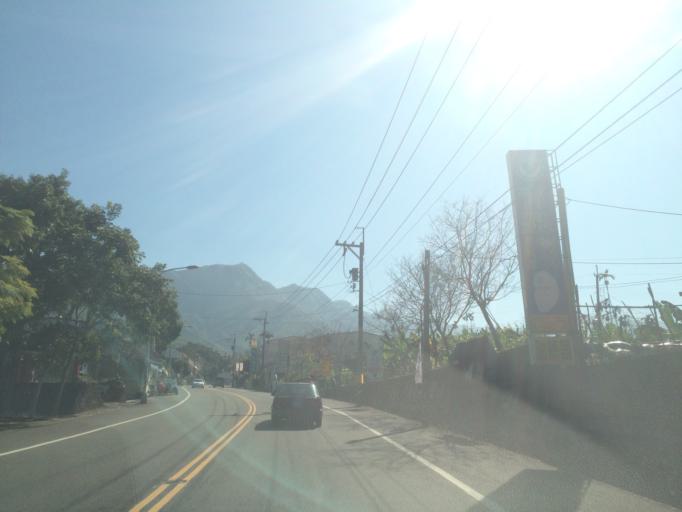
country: TW
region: Taiwan
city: Lugu
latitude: 23.7337
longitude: 120.7669
